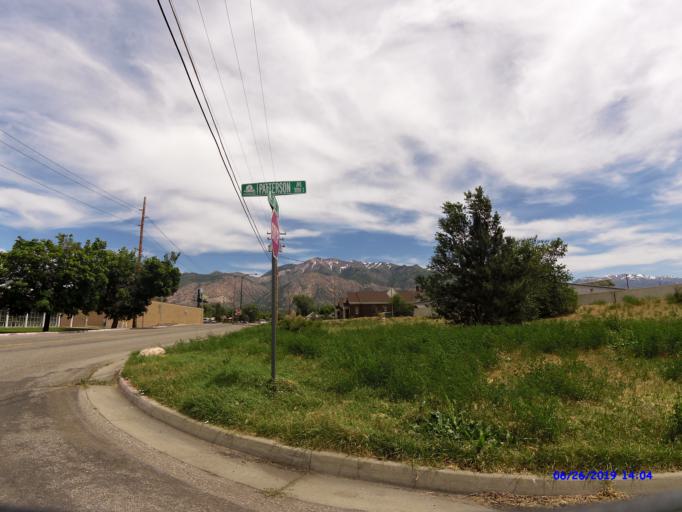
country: US
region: Utah
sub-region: Weber County
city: Ogden
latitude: 41.2102
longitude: -111.9815
